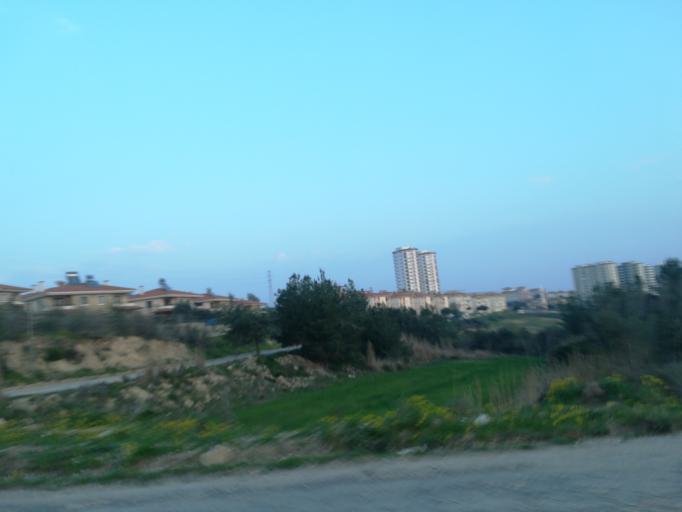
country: TR
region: Adana
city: Adana
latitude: 37.0820
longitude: 35.4096
